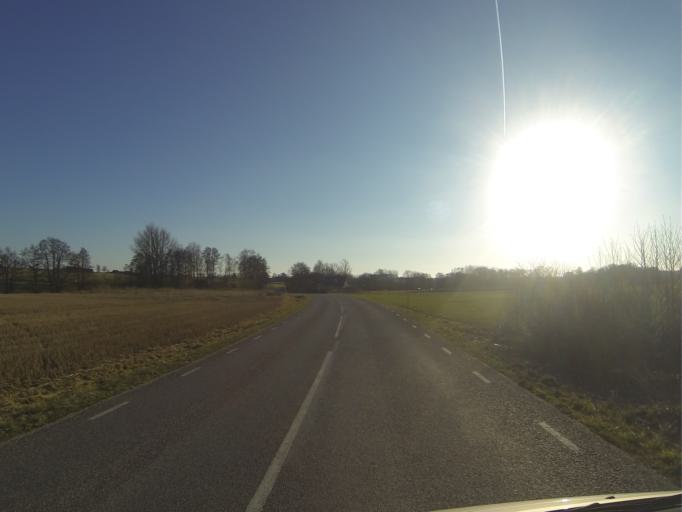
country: SE
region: Skane
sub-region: Hoors Kommun
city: Loberod
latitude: 55.7926
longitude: 13.5388
